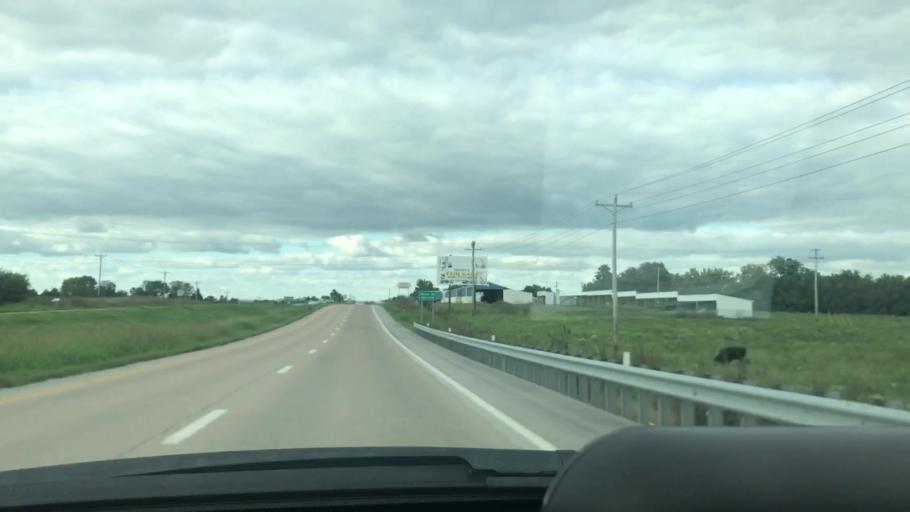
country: US
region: Missouri
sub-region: Benton County
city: Lincoln
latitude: 38.3296
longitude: -93.3415
